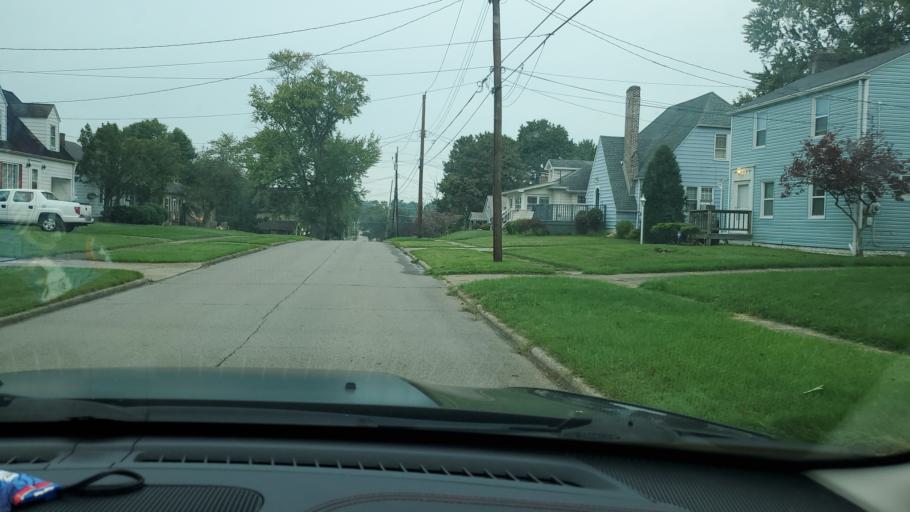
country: US
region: Ohio
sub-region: Mahoning County
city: Boardman
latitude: 41.0436
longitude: -80.6556
